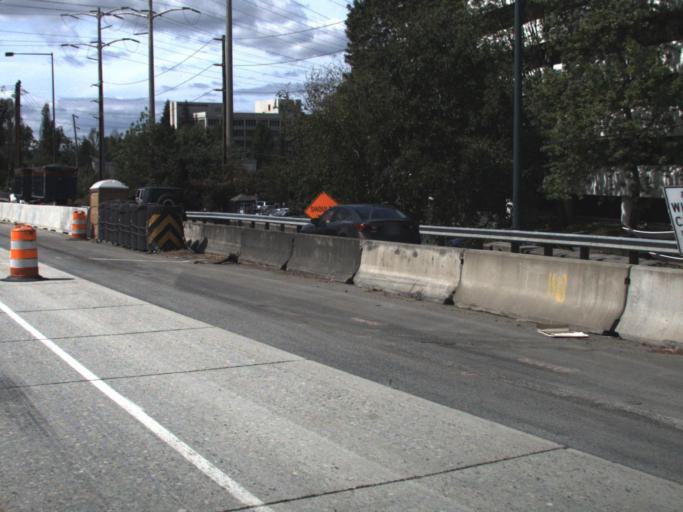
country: US
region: Washington
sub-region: King County
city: Renton
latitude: 47.4686
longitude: -122.2105
